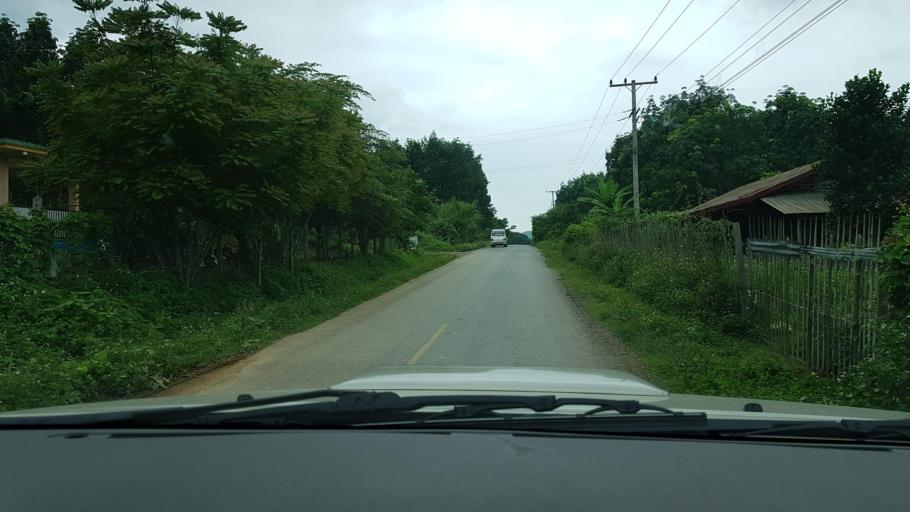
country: LA
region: Loungnamtha
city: Muang Nale
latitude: 20.2248
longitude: 101.5545
